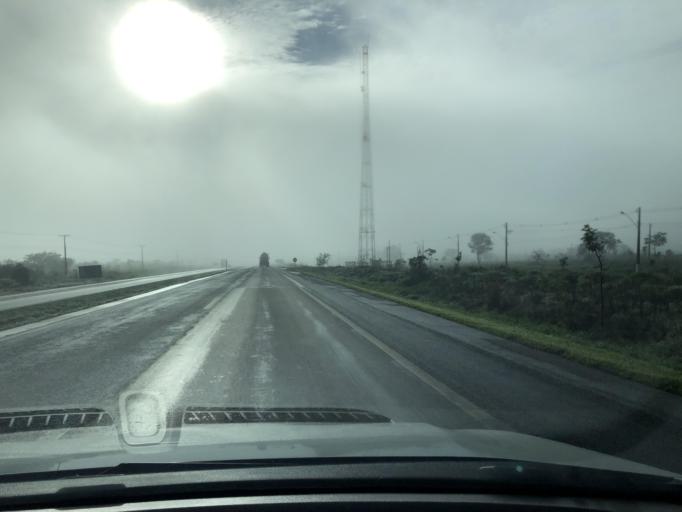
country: BR
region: Goias
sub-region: Luziania
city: Luziania
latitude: -16.2740
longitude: -47.8709
